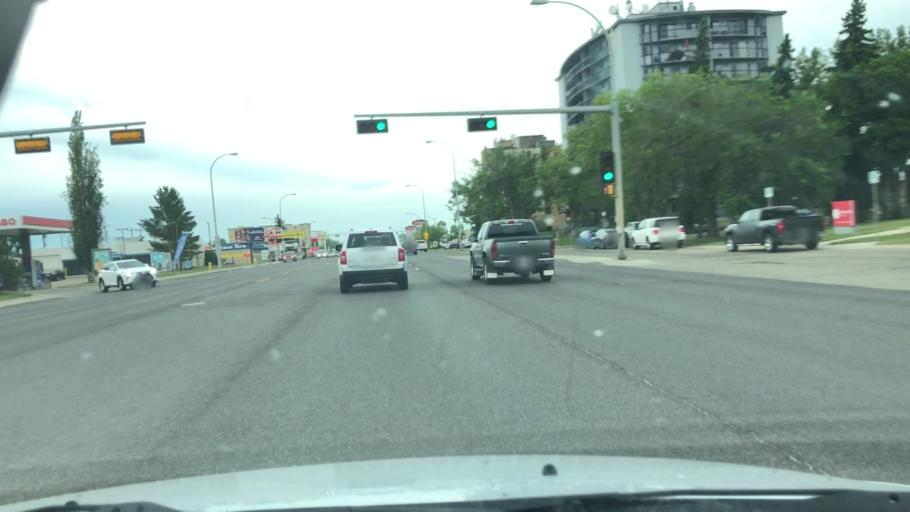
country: CA
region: Alberta
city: Edmonton
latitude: 53.5945
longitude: -113.4920
